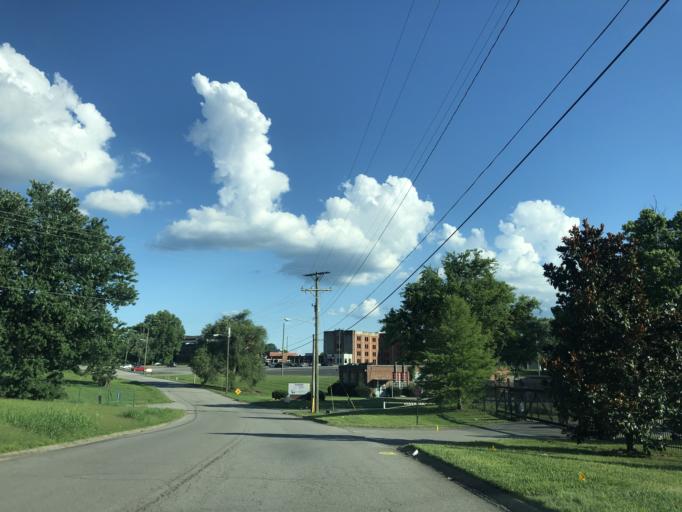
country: US
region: Tennessee
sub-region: Davidson County
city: Nashville
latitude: 36.1806
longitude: -86.8476
